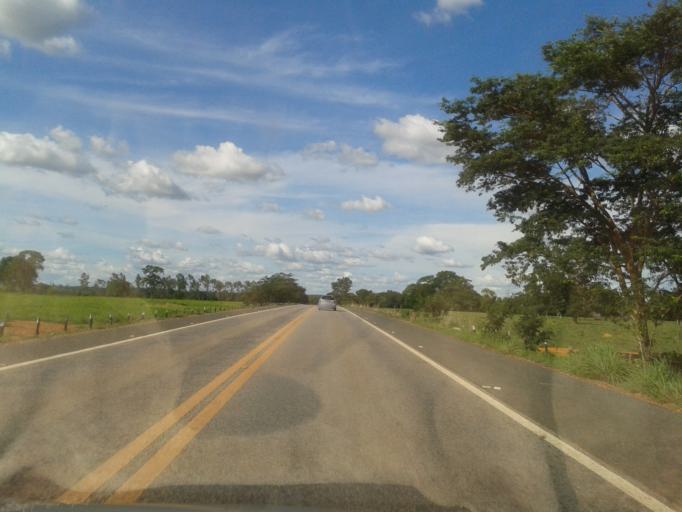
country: BR
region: Goias
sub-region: Mozarlandia
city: Mozarlandia
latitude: -15.0123
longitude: -50.5937
